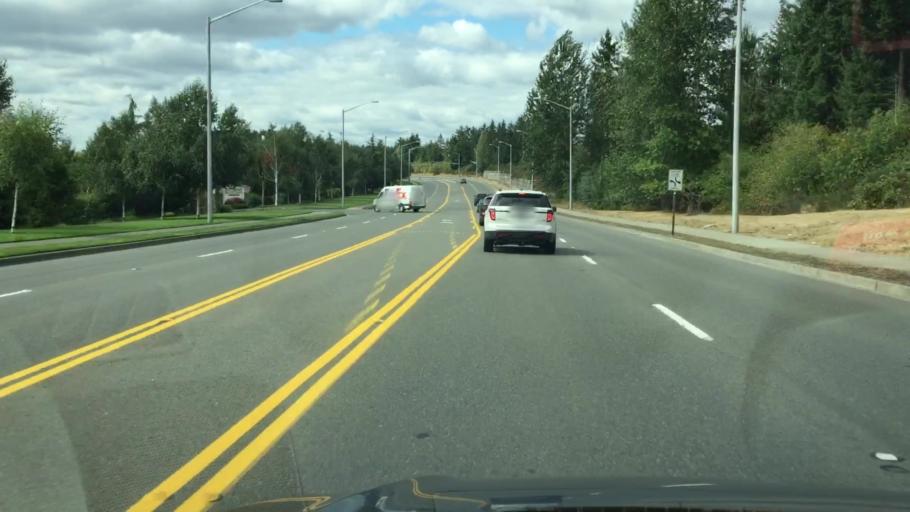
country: US
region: Washington
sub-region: Pierce County
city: South Hill
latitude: 47.0974
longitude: -122.2780
